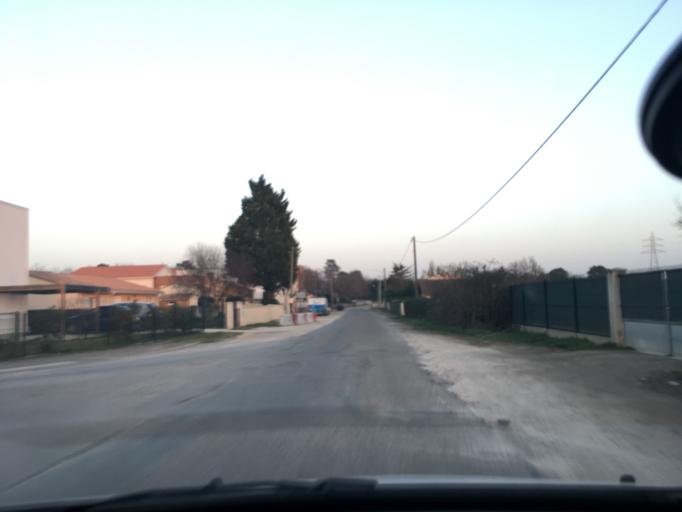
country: FR
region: Aquitaine
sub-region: Departement de la Gironde
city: Le Taillan-Medoc
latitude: 44.9040
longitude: -0.6888
